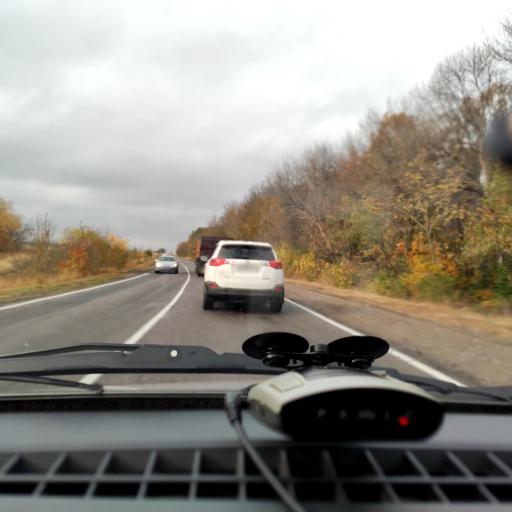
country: RU
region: Voronezj
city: Kolodeznyy
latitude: 51.3788
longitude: 39.0181
